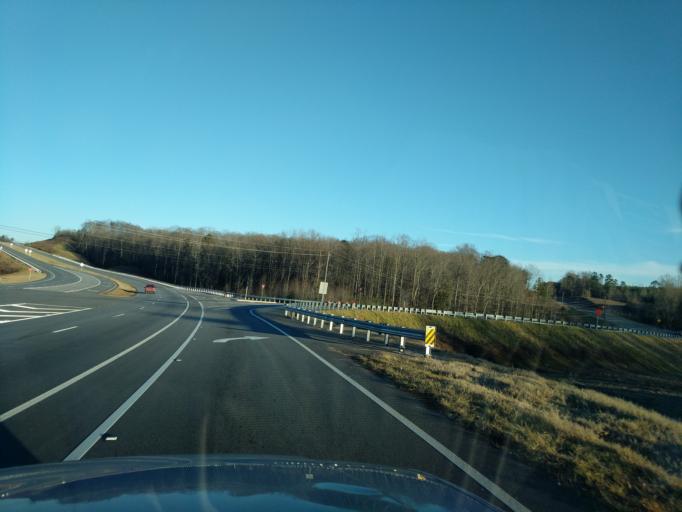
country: US
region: Georgia
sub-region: Stephens County
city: Toccoa
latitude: 34.5204
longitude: -83.2387
